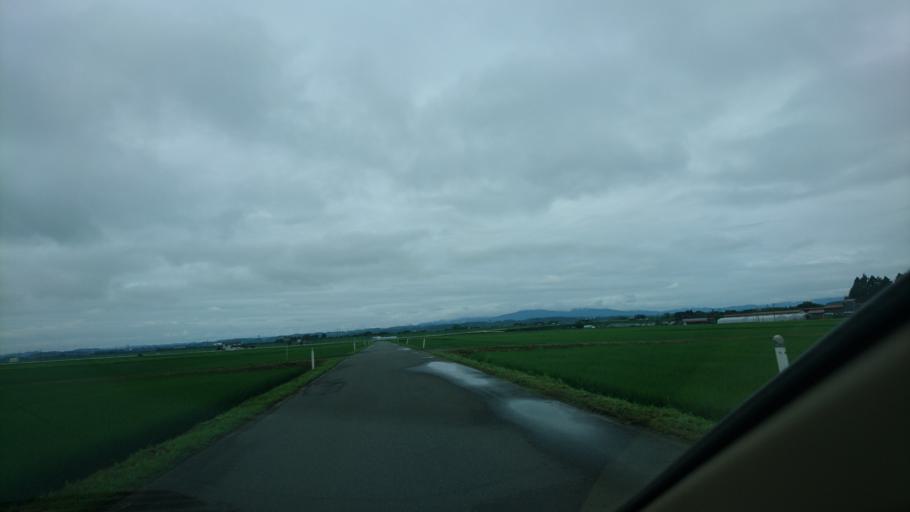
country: JP
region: Iwate
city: Mizusawa
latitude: 39.0636
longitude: 141.1748
